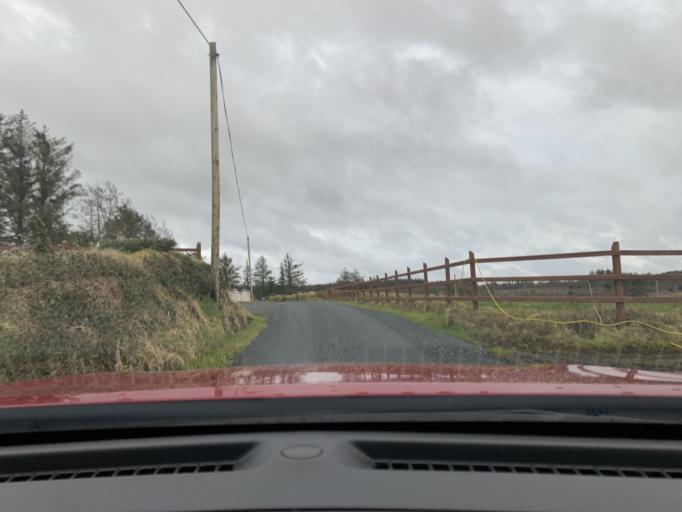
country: IE
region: Connaught
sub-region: Roscommon
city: Ballaghaderreen
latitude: 53.9667
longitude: -8.5153
